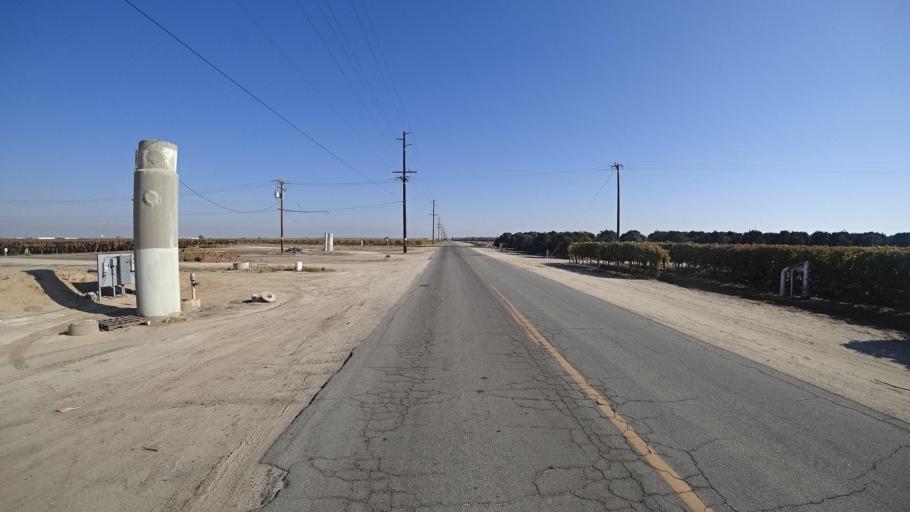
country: US
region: California
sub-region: Kern County
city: McFarland
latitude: 35.7035
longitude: -119.1701
